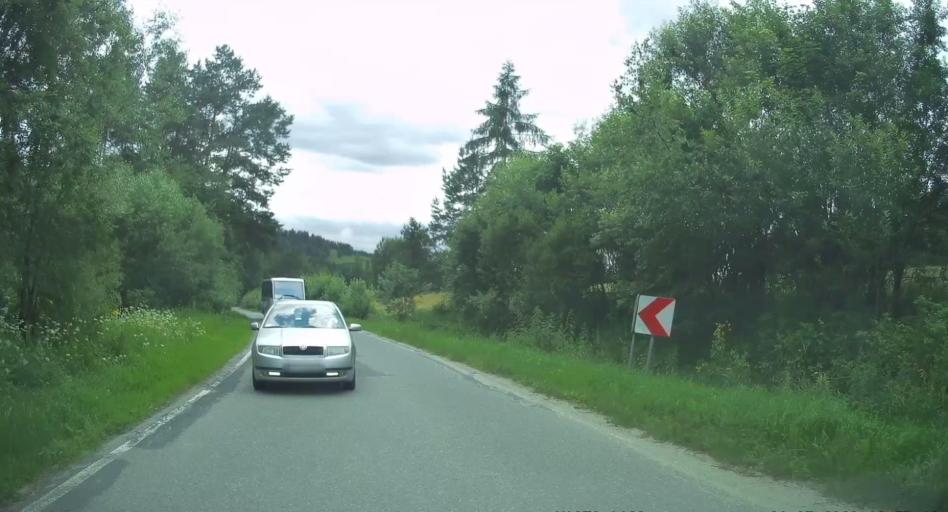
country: PL
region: Lesser Poland Voivodeship
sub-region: Powiat nowosadecki
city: Muszyna
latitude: 49.3884
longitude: 20.9025
